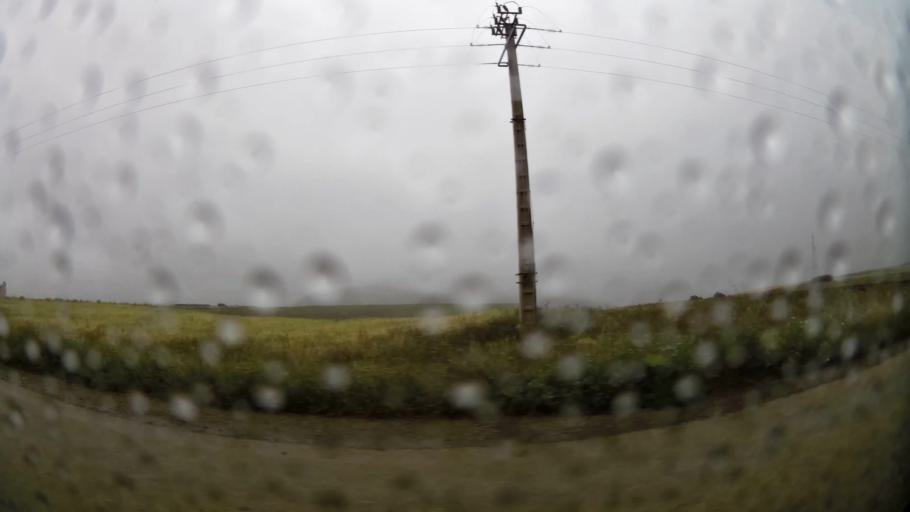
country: MA
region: Oriental
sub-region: Nador
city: Boudinar
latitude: 35.1291
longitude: -3.6471
